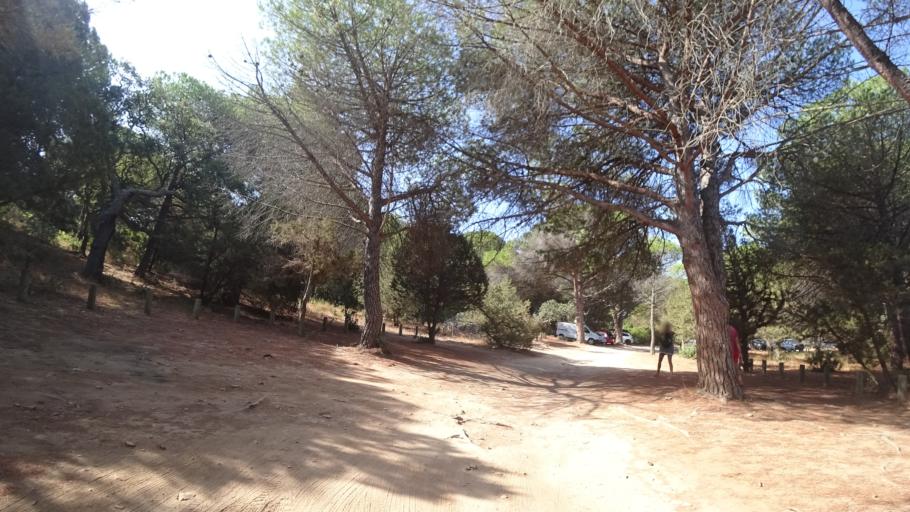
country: FR
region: Corsica
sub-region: Departement de la Corse-du-Sud
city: Porto-Vecchio
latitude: 41.5615
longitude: 9.3374
